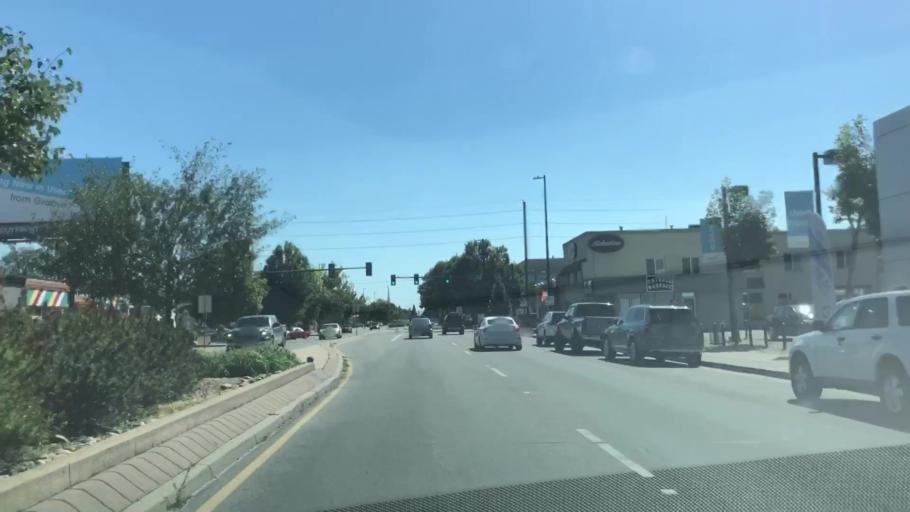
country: US
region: Colorado
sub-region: Arapahoe County
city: Englewood
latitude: 39.6648
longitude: -104.9877
